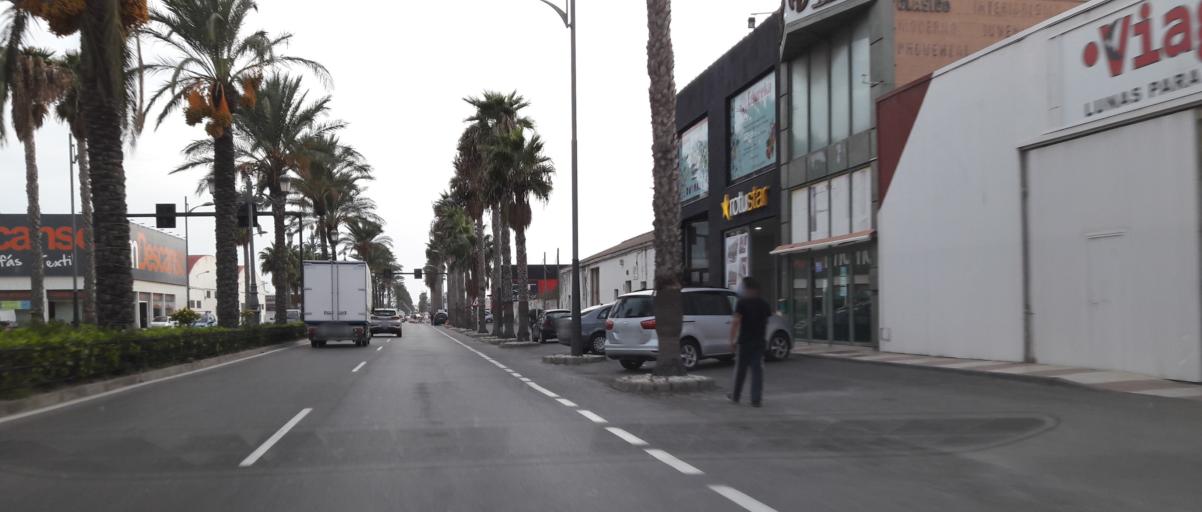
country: ES
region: Andalusia
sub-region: Provincia de Almeria
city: Roquetas de Mar
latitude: 36.7814
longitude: -2.6087
